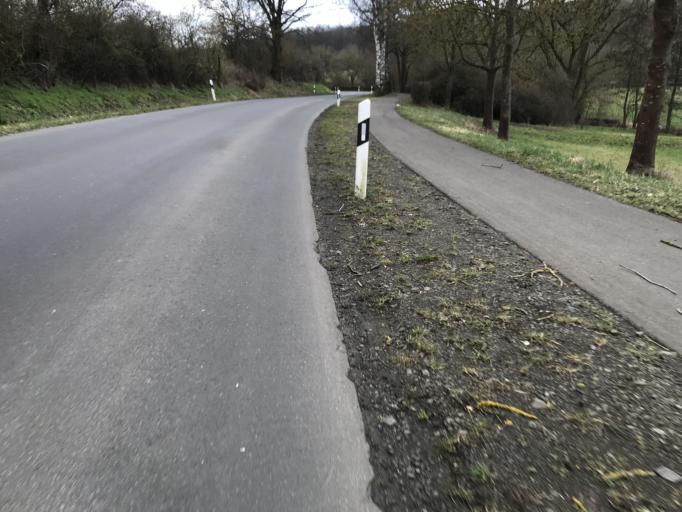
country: DE
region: Hesse
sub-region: Regierungsbezirk Giessen
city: Lich
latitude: 50.5465
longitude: 8.7893
